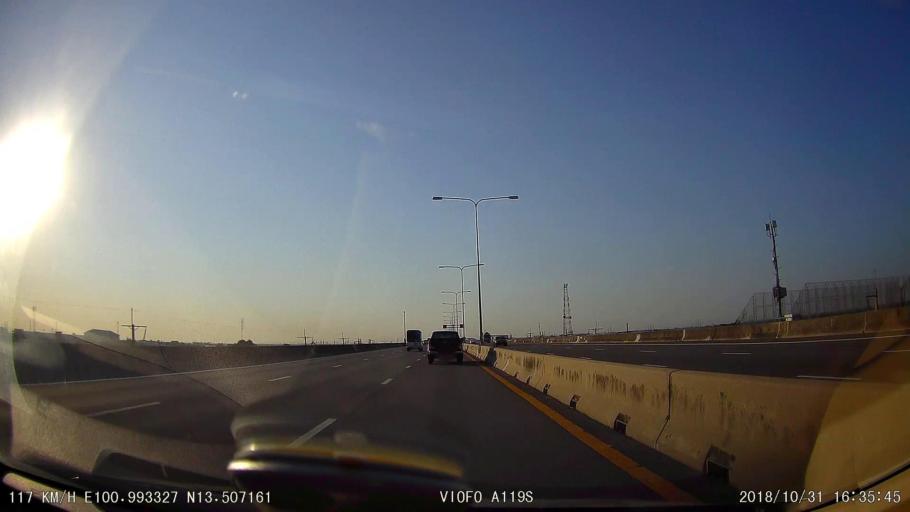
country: TH
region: Chachoengsao
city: Bang Pakong
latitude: 13.5062
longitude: 100.9937
